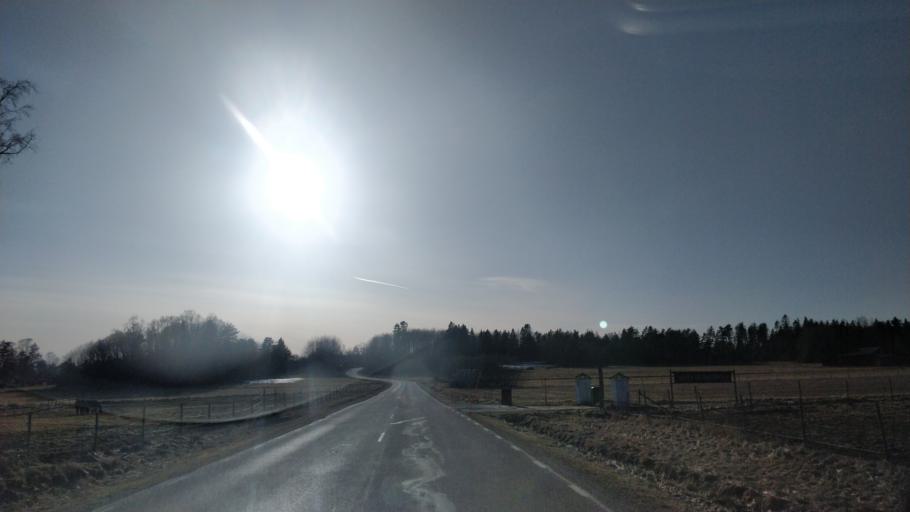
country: SE
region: Uppsala
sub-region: Enkopings Kommun
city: Orsundsbro
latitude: 59.7503
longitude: 17.2524
